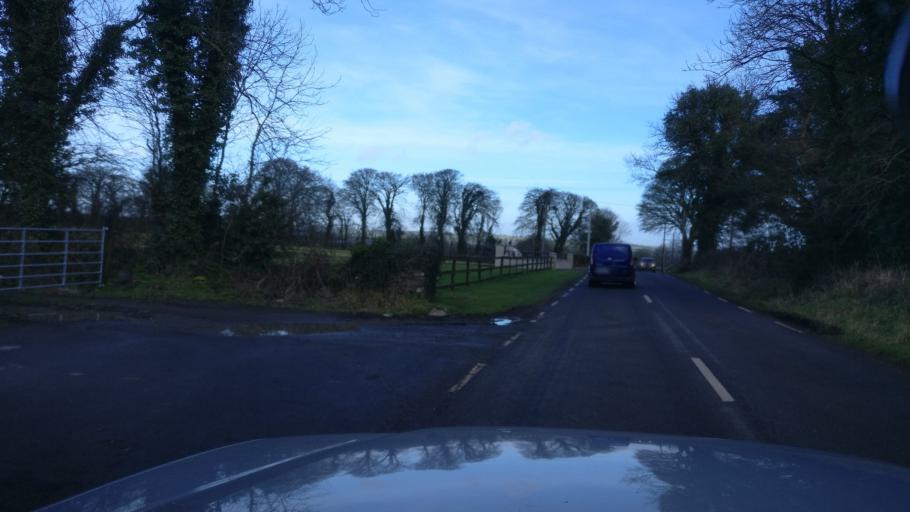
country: IE
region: Leinster
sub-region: Kilkenny
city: Castlecomer
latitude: 52.8396
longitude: -7.1892
